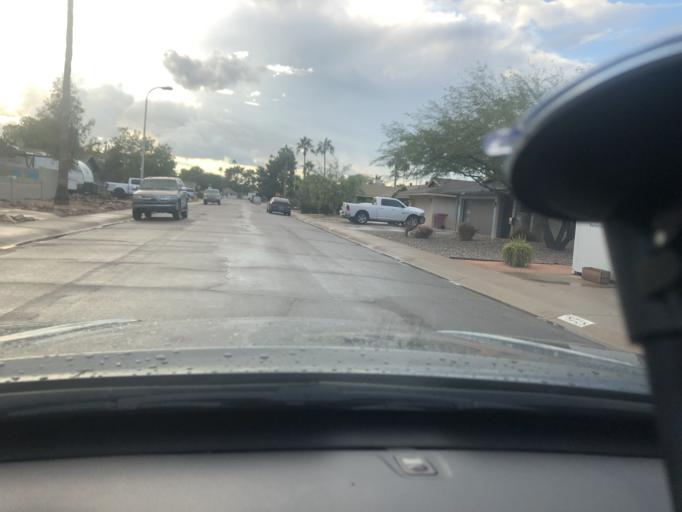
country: US
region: Arizona
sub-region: Maricopa County
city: Scottsdale
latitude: 33.4867
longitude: -111.8929
